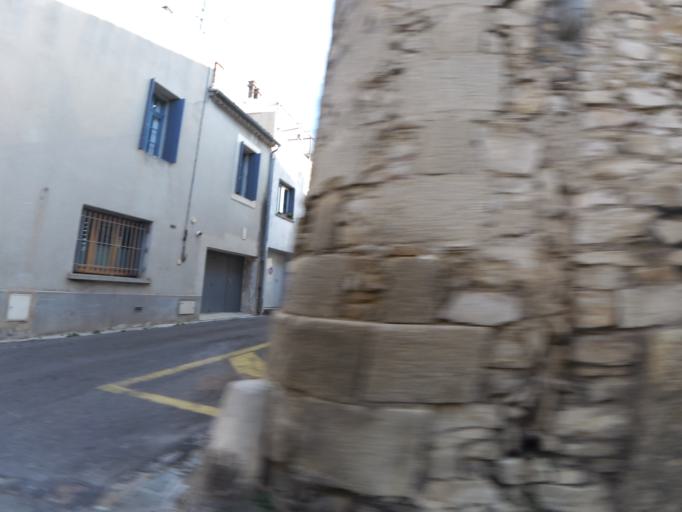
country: FR
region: Languedoc-Roussillon
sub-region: Departement de l'Herault
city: Lunel
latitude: 43.6727
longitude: 4.1327
